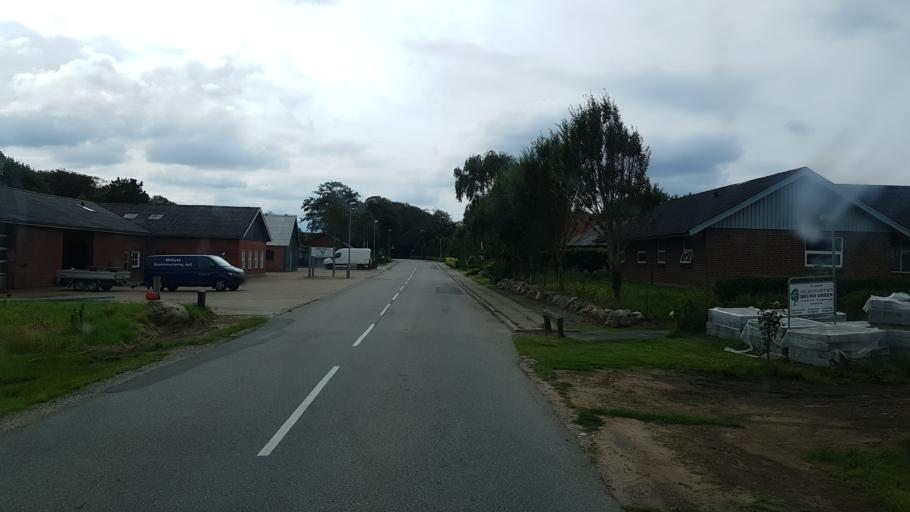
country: DK
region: South Denmark
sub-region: Varde Kommune
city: Varde
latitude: 55.7629
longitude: 8.4330
